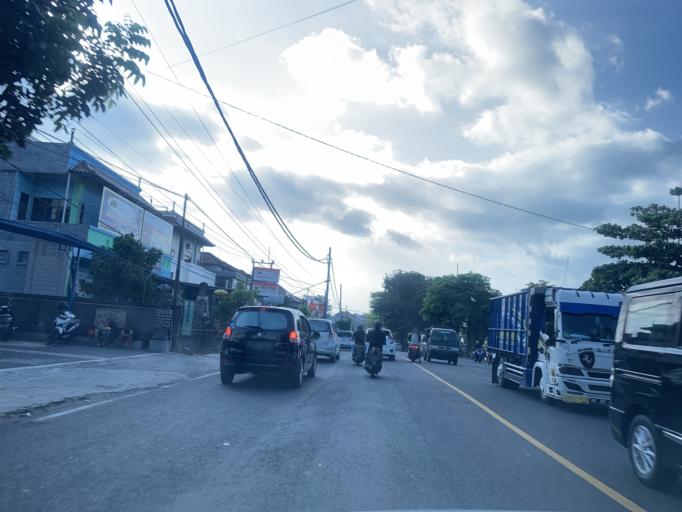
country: ID
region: Bali
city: Banjar Tegal Belodan
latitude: -8.5479
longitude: 115.1193
